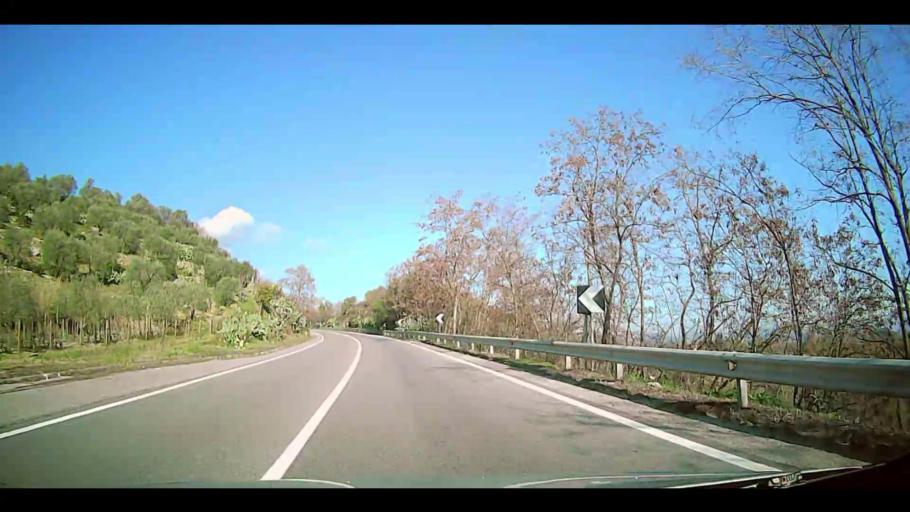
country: IT
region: Calabria
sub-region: Provincia di Crotone
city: Caccuri
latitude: 39.2003
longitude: 16.8118
